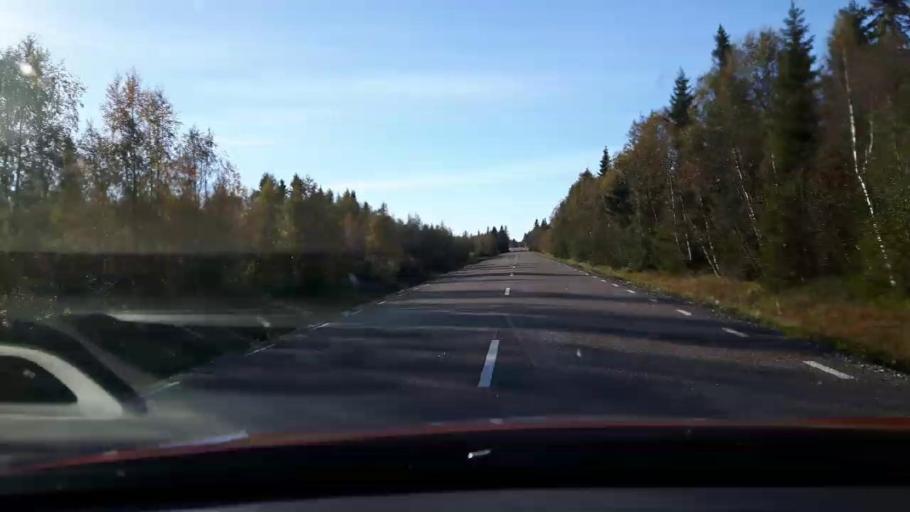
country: SE
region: Jaemtland
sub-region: Stroemsunds Kommun
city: Stroemsund
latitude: 63.8611
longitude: 15.1757
